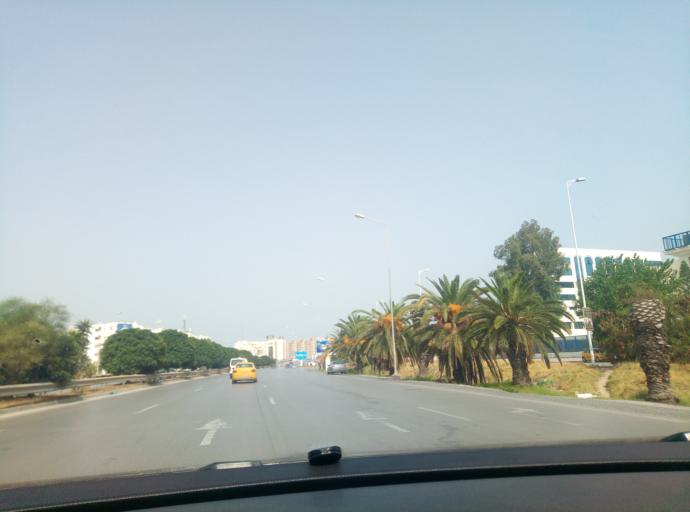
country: TN
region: Ariana
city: Ariana
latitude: 36.8508
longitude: 10.1904
